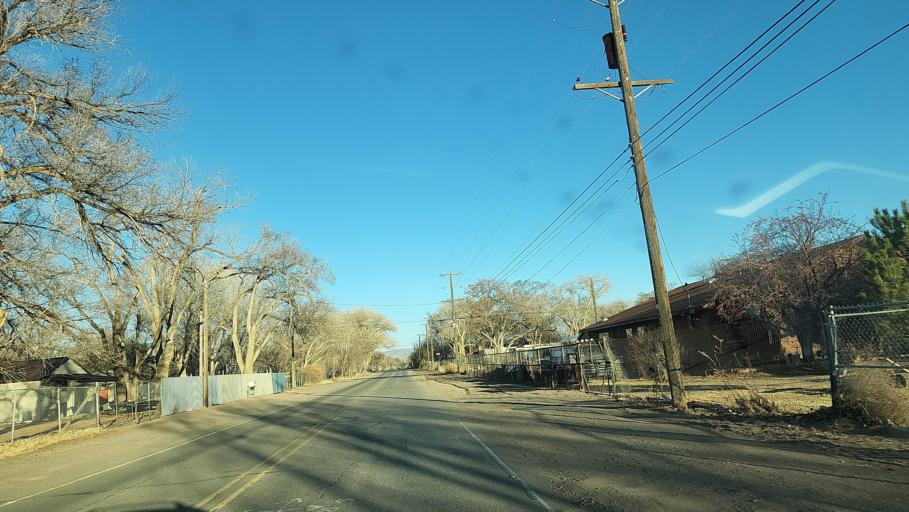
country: US
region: New Mexico
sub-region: Bernalillo County
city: South Valley
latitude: 35.0305
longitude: -106.7054
